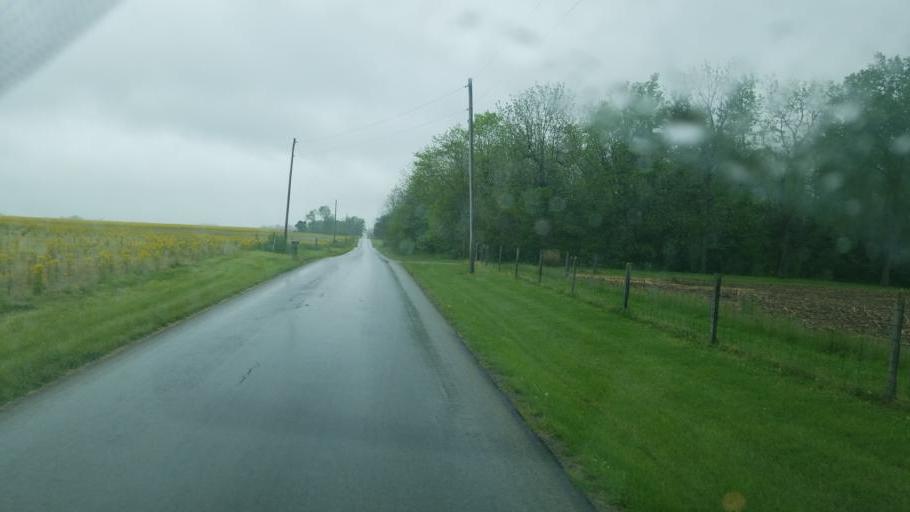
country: US
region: Ohio
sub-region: Highland County
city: Greenfield
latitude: 39.3221
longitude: -83.4222
